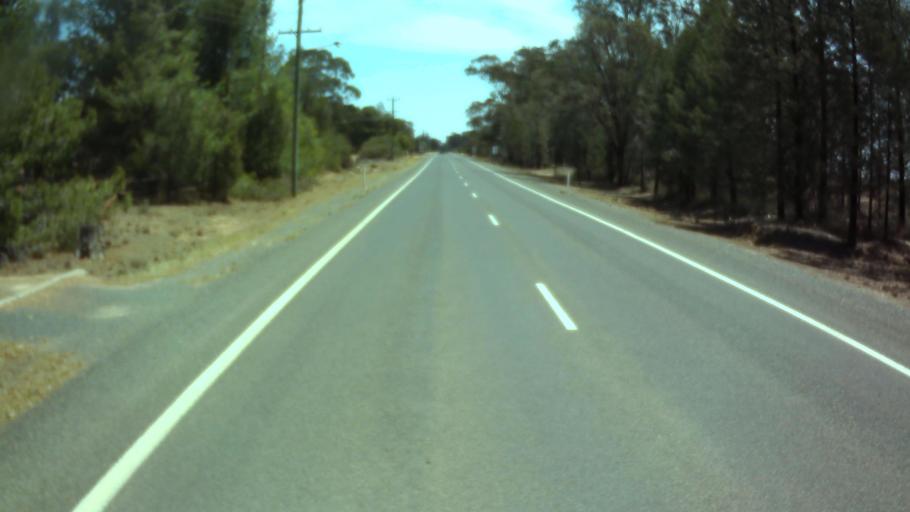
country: AU
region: New South Wales
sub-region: Weddin
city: Grenfell
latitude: -33.8434
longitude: 147.7349
